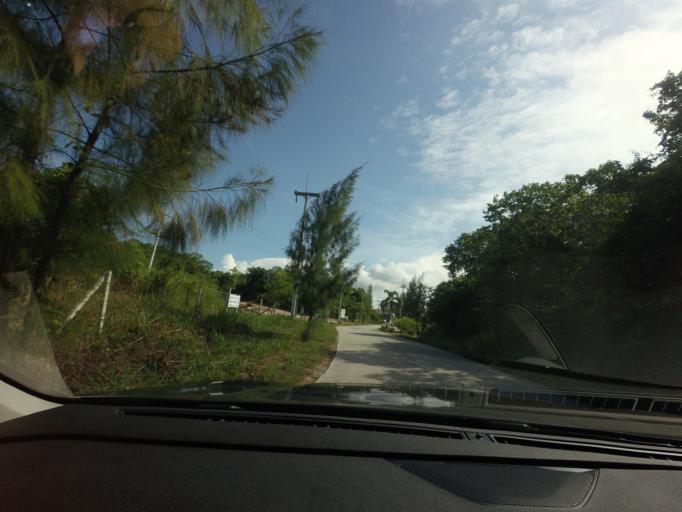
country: TH
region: Prachuap Khiri Khan
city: Hua Hin
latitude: 12.4805
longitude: 99.9373
